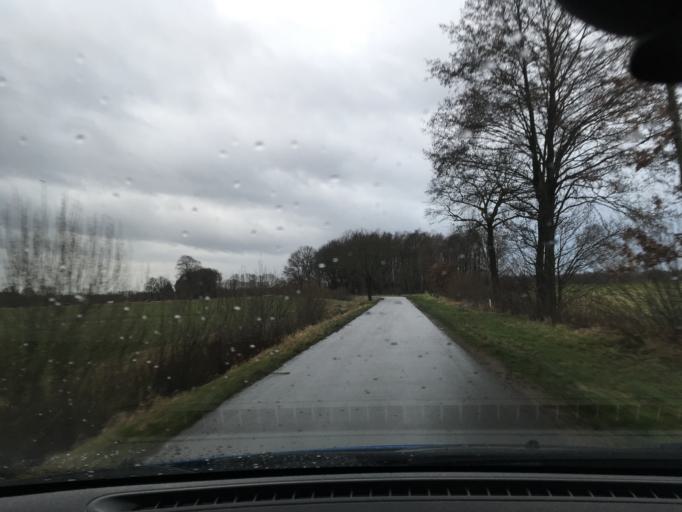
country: DE
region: Lower Saxony
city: Hittbergen
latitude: 53.3210
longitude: 10.6394
